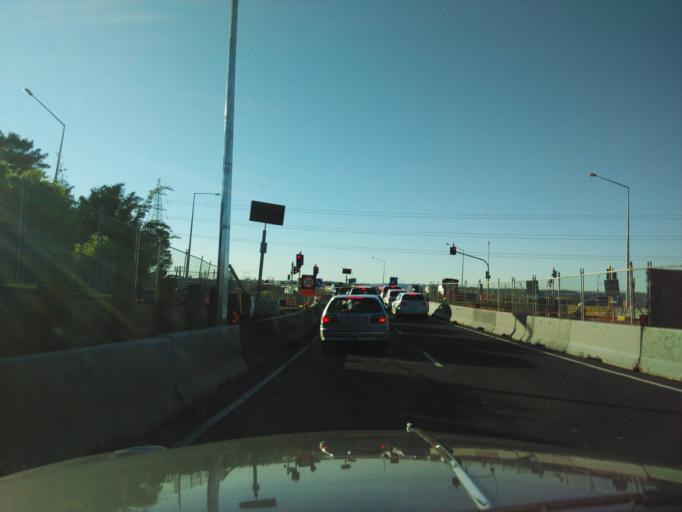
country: NZ
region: Auckland
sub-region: Auckland
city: Rosebank
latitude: -36.8588
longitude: 174.6520
